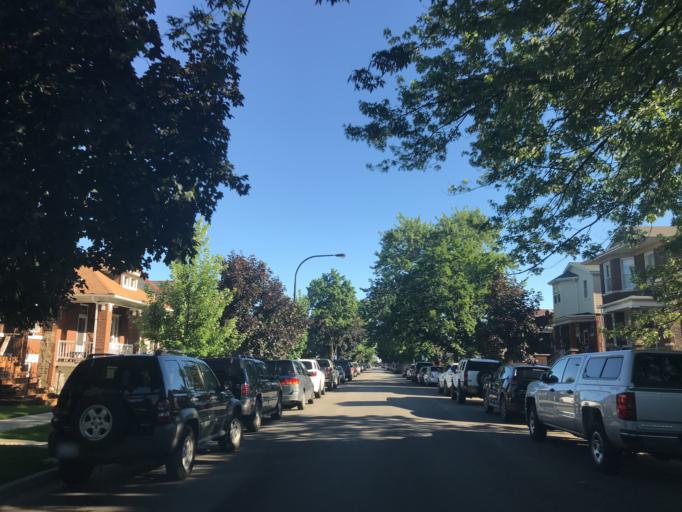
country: US
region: Illinois
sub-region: Cook County
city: Cicero
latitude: 41.8474
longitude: -87.7662
